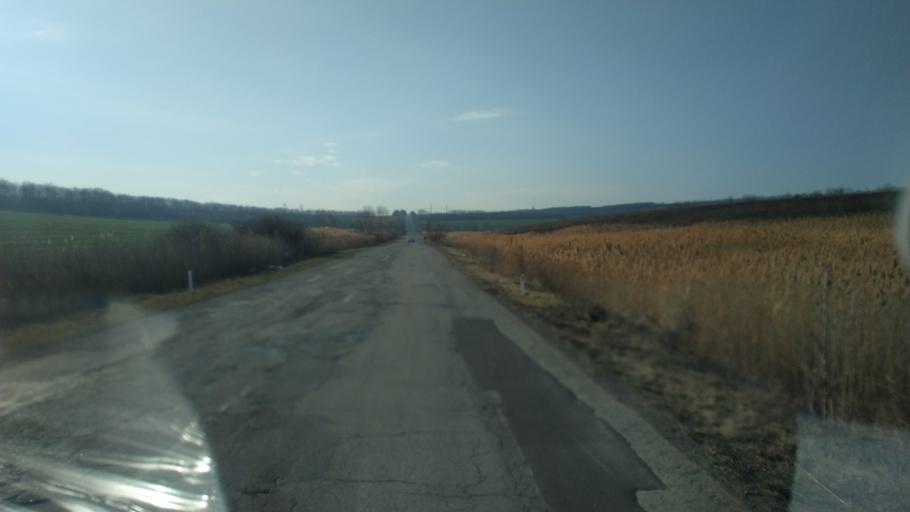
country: MD
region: Chisinau
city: Singera
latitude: 46.8844
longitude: 29.0393
